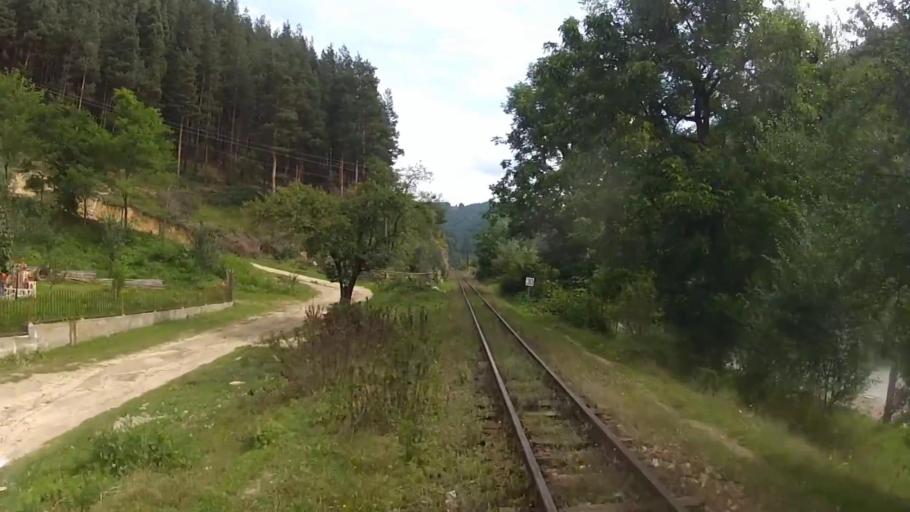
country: BG
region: Blagoevgrad
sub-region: Obshtina Yakoruda
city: Yakoruda
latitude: 42.0518
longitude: 23.7300
